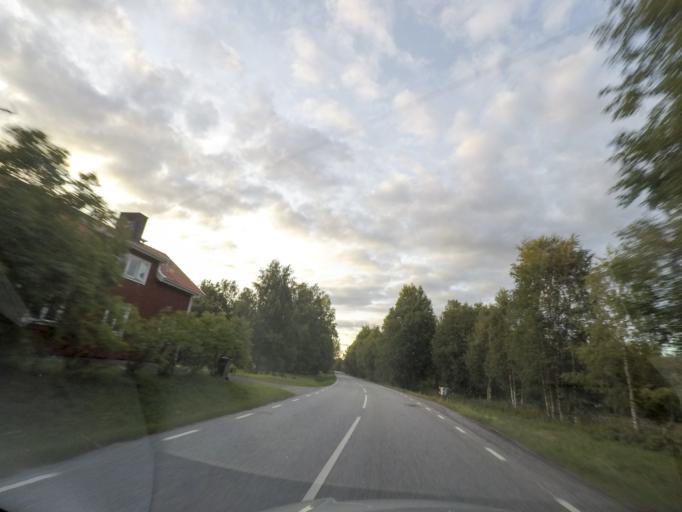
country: SE
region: OErebro
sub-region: Hallefors Kommun
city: Haellefors
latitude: 59.8066
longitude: 14.5023
